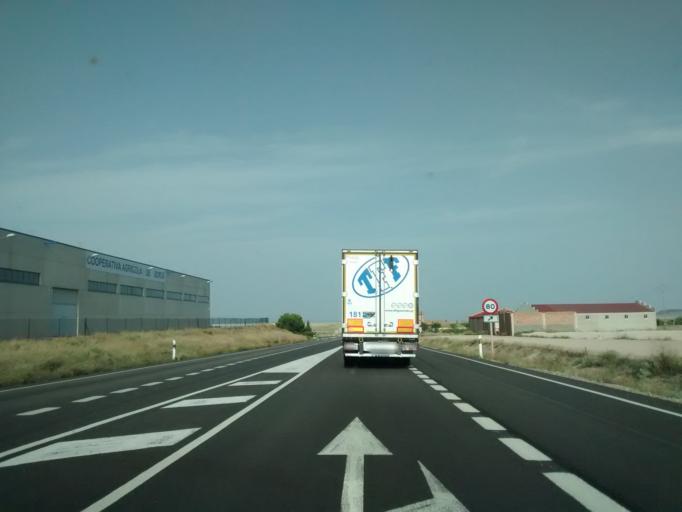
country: ES
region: Aragon
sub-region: Provincia de Zaragoza
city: Albeta
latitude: 41.8310
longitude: -1.5057
